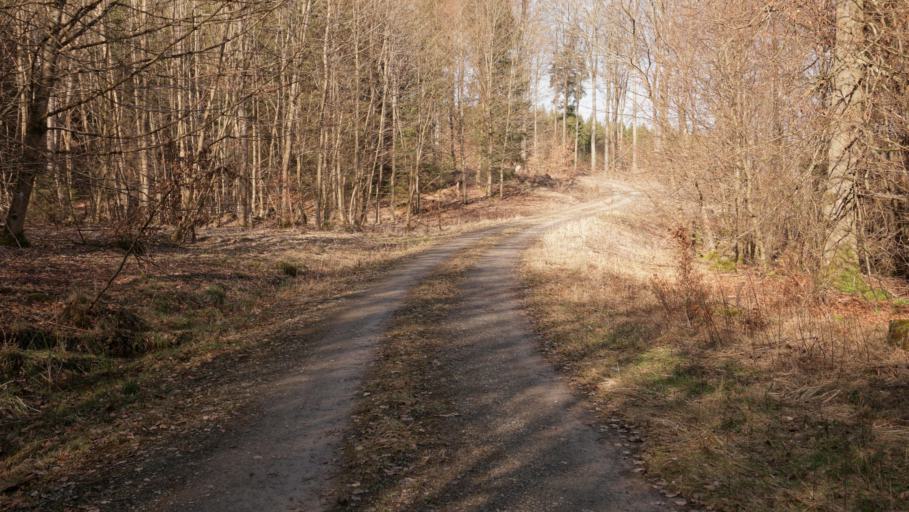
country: DE
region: Baden-Wuerttemberg
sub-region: Karlsruhe Region
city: Fahrenbach
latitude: 49.4477
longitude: 9.1234
